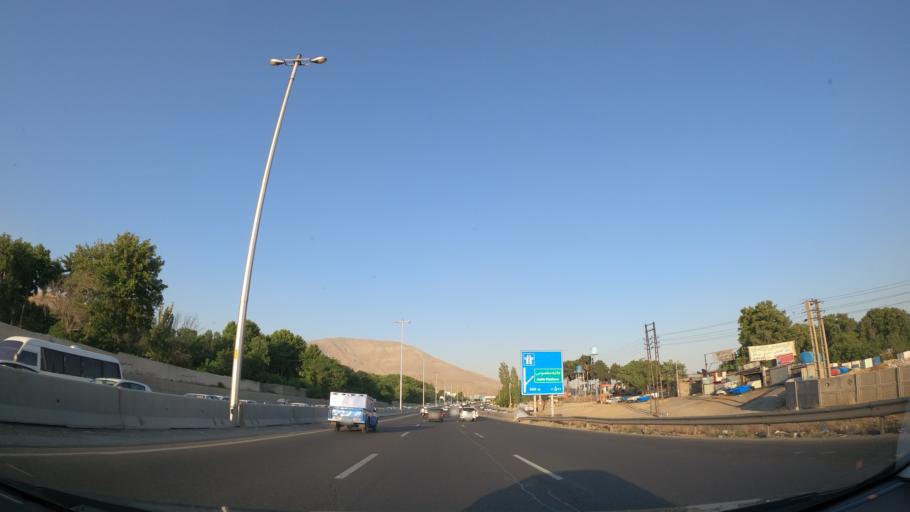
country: IR
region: Alborz
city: Karaj
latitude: 35.7902
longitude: 51.0106
